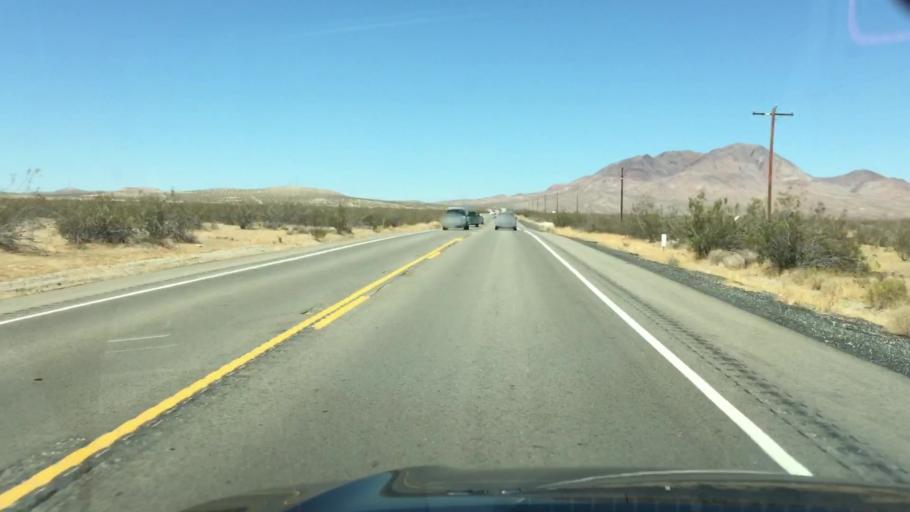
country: US
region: California
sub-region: Kern County
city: Boron
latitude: 35.2888
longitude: -117.6158
